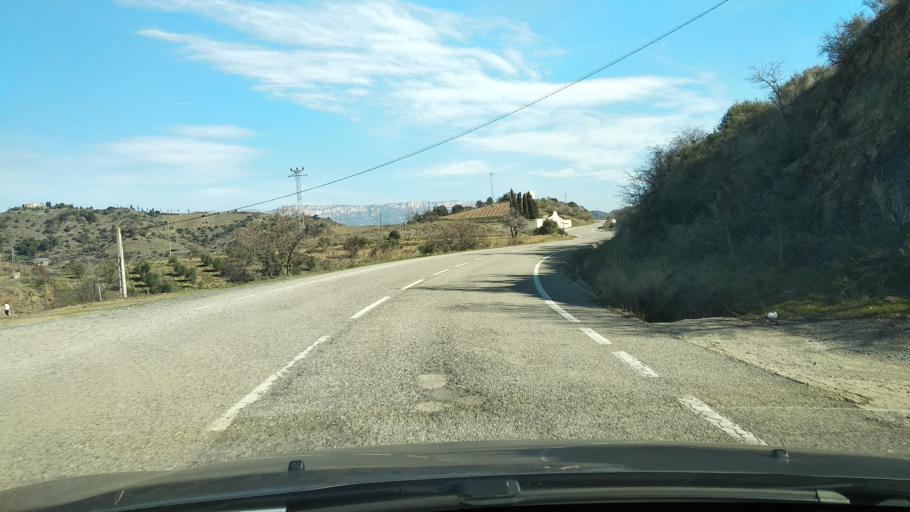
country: ES
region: Catalonia
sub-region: Provincia de Tarragona
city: Falset
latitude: 41.1950
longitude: 0.7770
